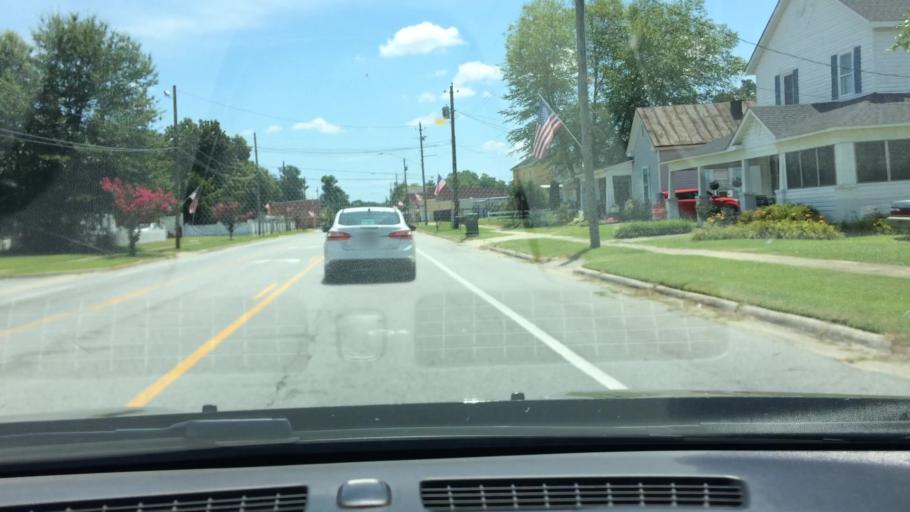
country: US
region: North Carolina
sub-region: Beaufort County
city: Washington
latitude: 35.5639
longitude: -77.1930
